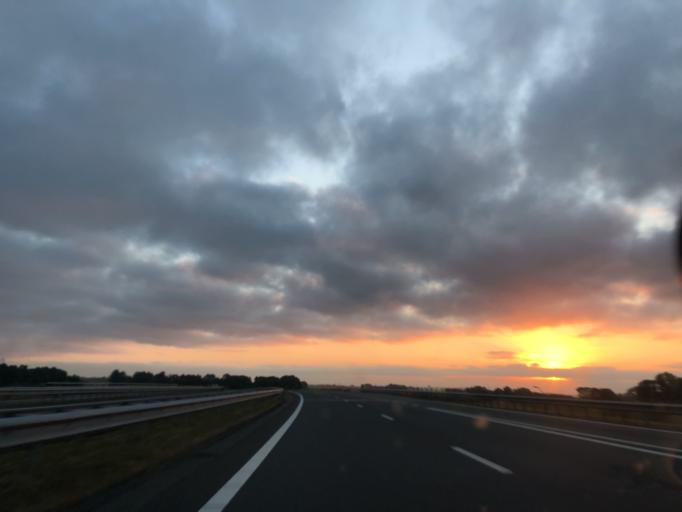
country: NL
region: Groningen
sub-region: Gemeente Veendam
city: Veendam
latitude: 53.0974
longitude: 6.8962
